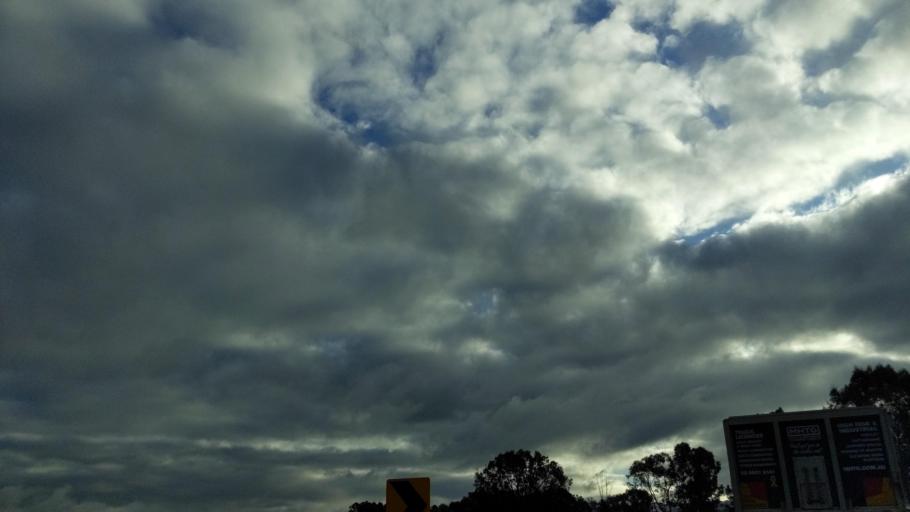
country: AU
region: New South Wales
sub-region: Wagga Wagga
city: Wagga Wagga
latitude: -35.0708
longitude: 147.3809
